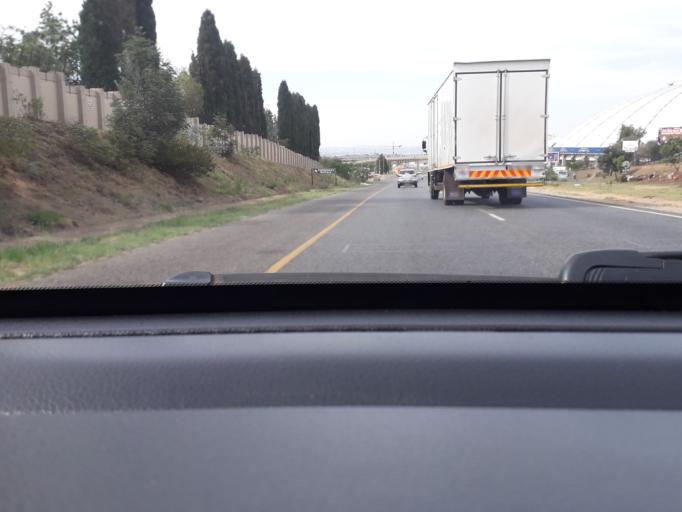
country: ZA
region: Gauteng
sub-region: West Rand District Municipality
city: Muldersdriseloop
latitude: -26.0659
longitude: 27.9403
